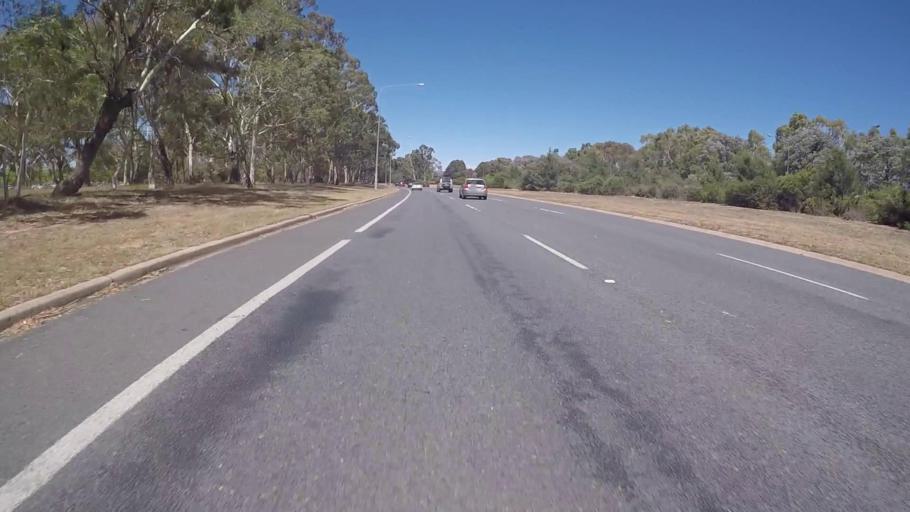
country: AU
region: Australian Capital Territory
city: Macarthur
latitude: -35.3820
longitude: 149.0575
